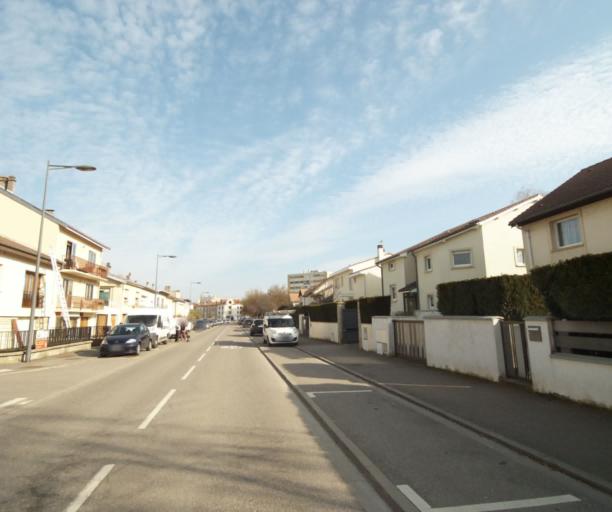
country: FR
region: Lorraine
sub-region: Departement de Meurthe-et-Moselle
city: Villers-les-Nancy
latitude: 48.6755
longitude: 6.1556
